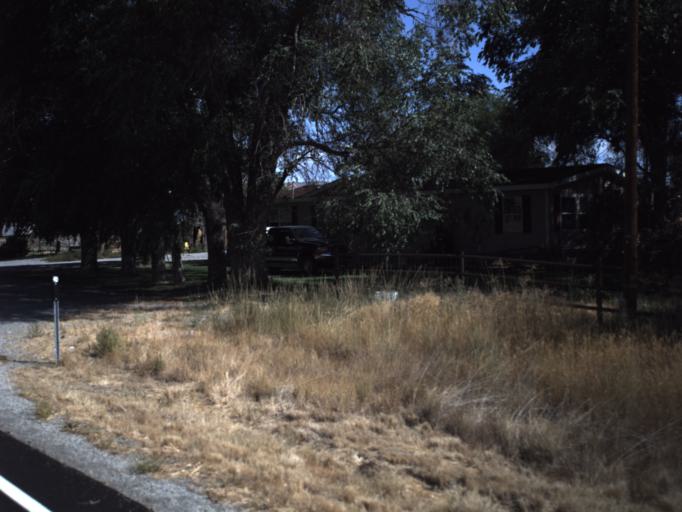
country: US
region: Utah
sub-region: Box Elder County
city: Garland
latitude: 41.7808
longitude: -112.4353
